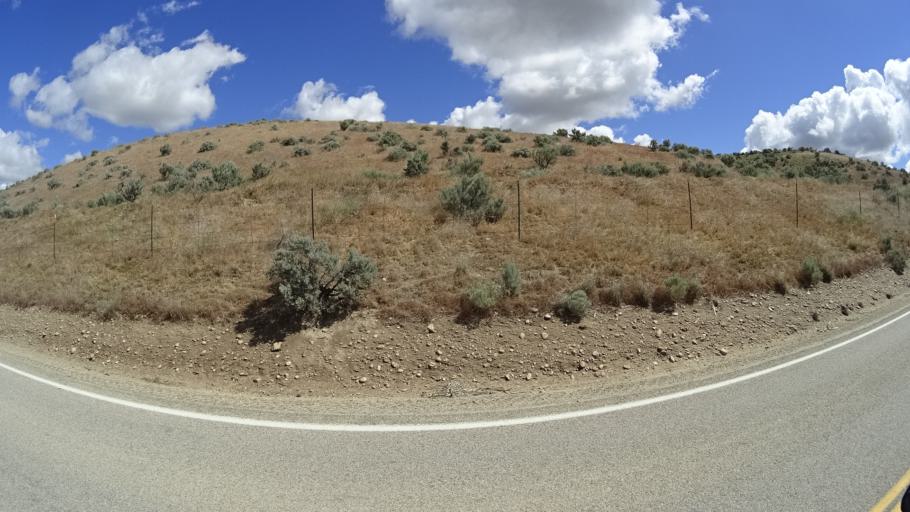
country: US
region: Idaho
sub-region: Ada County
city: Kuna
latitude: 43.5079
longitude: -116.3077
